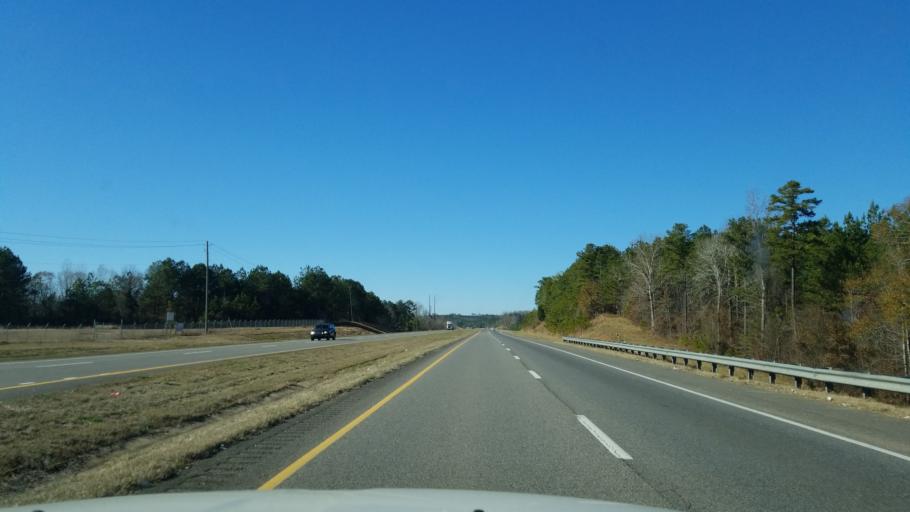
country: US
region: Alabama
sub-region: Tuscaloosa County
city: Northport
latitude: 33.2585
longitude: -87.6991
